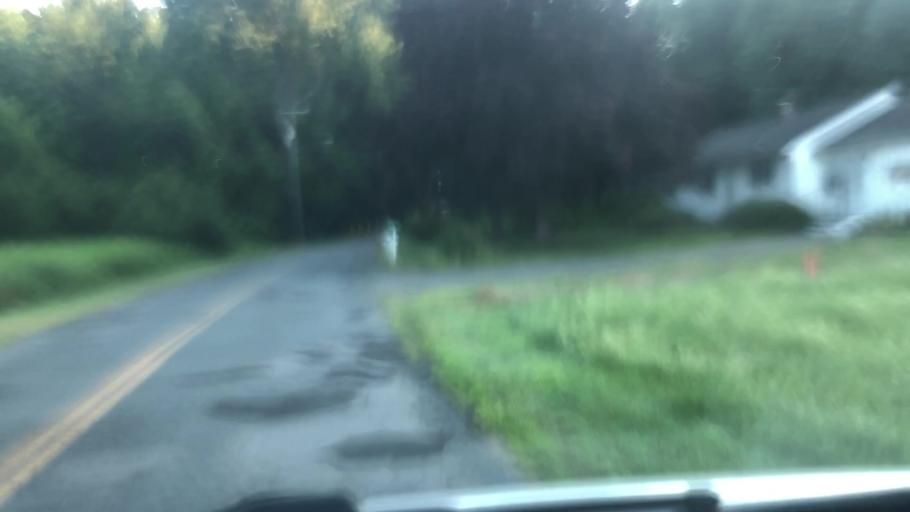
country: US
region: Massachusetts
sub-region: Hampshire County
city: Easthampton
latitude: 42.2794
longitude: -72.7161
